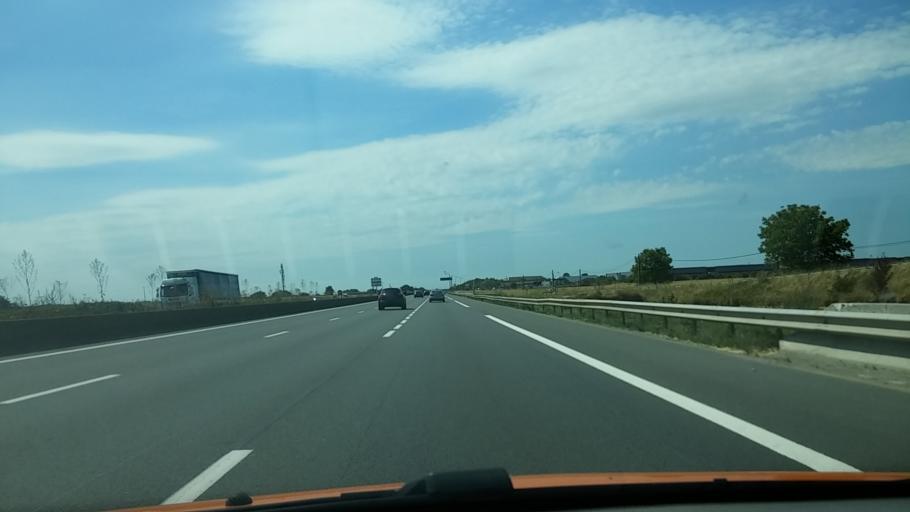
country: FR
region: Ile-de-France
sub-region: Departement de Seine-et-Marne
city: Chanteloup-en-Brie
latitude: 48.8306
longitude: 2.7555
